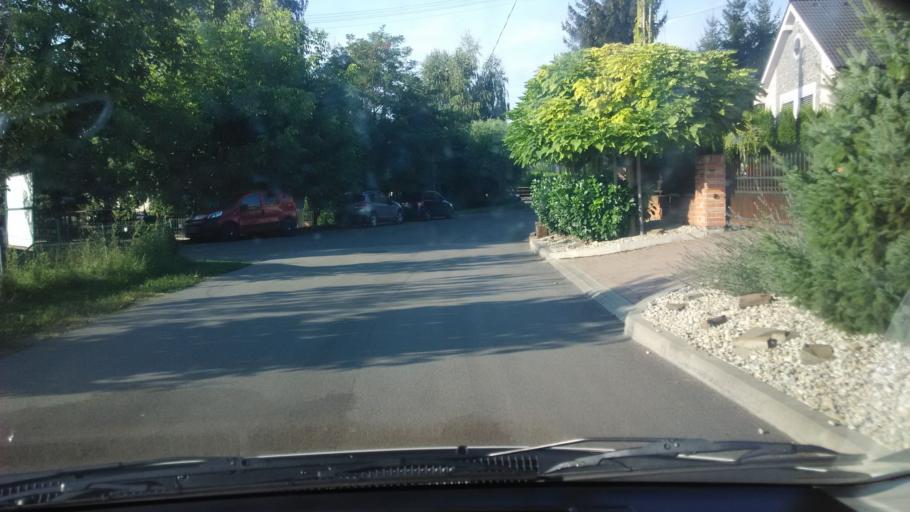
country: SK
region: Nitriansky
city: Levice
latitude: 48.2086
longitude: 18.6233
